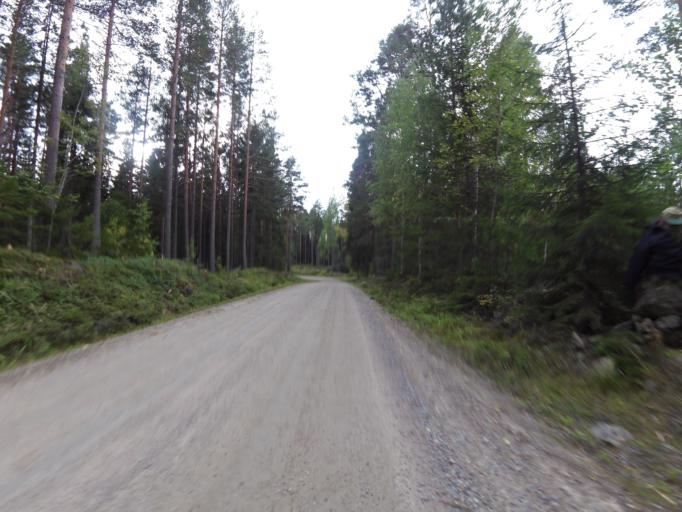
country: SE
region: Gaevleborg
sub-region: Sandvikens Kommun
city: Sandviken
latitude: 60.7473
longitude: 16.8405
